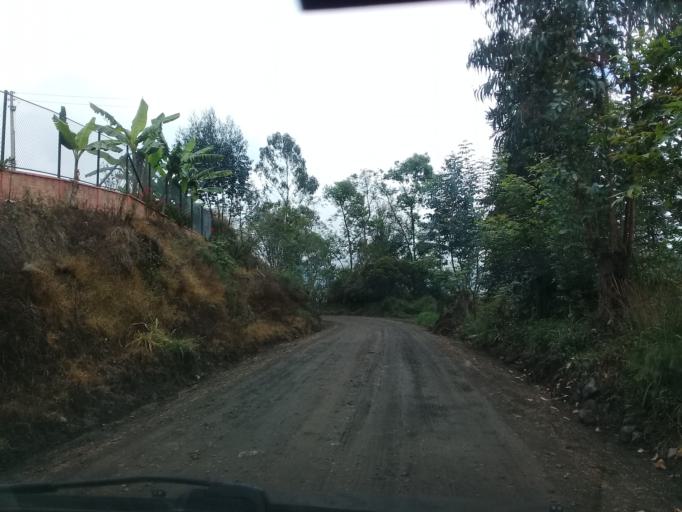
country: CO
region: Cundinamarca
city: Caqueza
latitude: 4.3976
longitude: -73.9839
